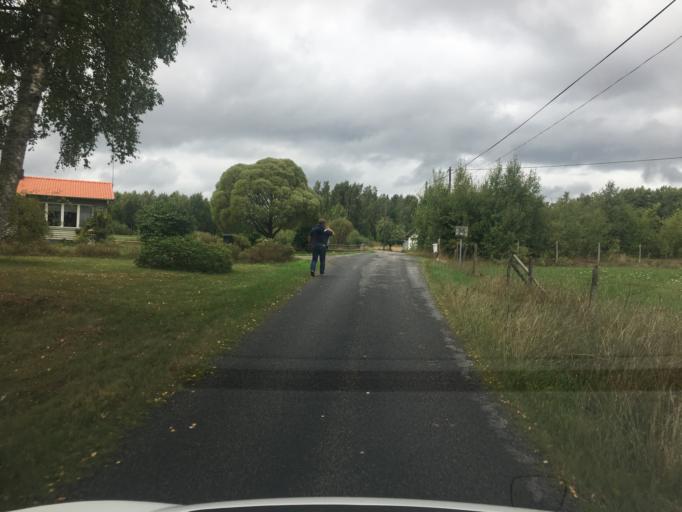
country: SE
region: Kronoberg
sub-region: Ljungby Kommun
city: Lagan
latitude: 56.9328
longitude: 14.0254
